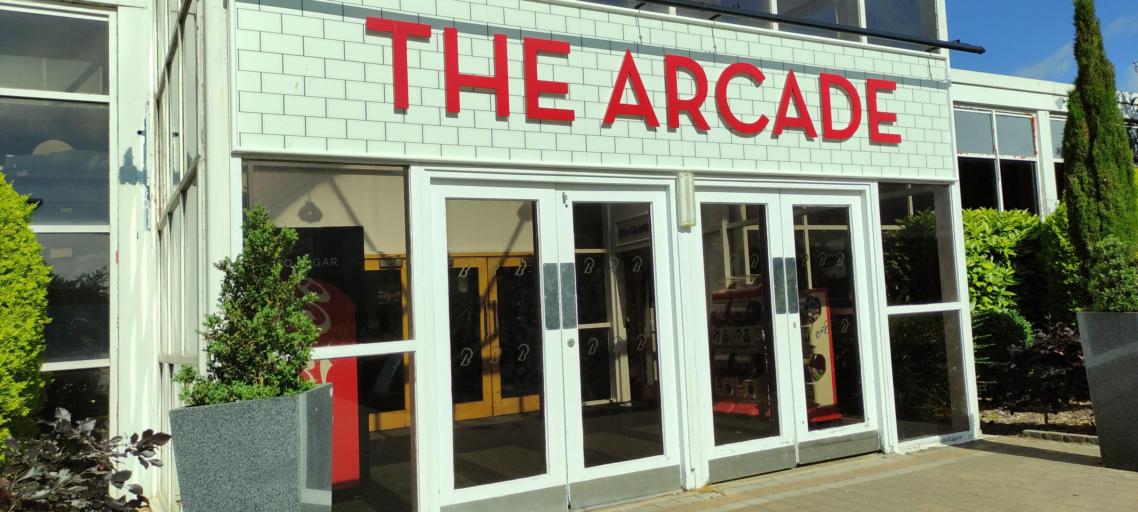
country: GB
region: England
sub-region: Lincolnshire
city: Ingoldmells
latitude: 53.1781
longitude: 0.3505
